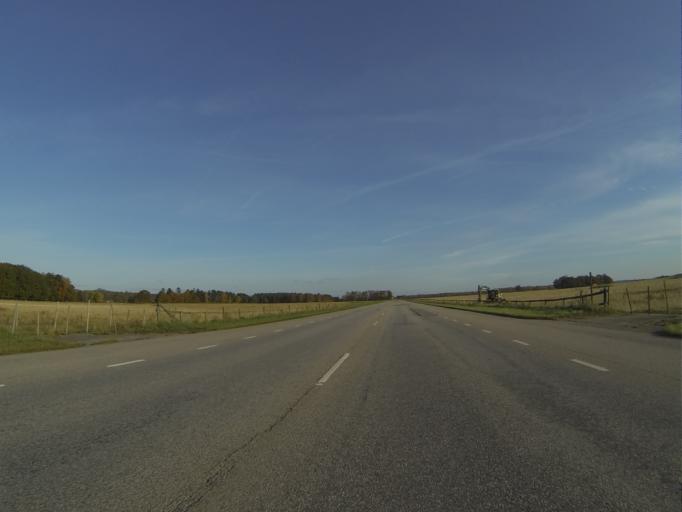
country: SE
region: Skane
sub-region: Hoors Kommun
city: Loberod
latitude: 55.7283
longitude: 13.4301
